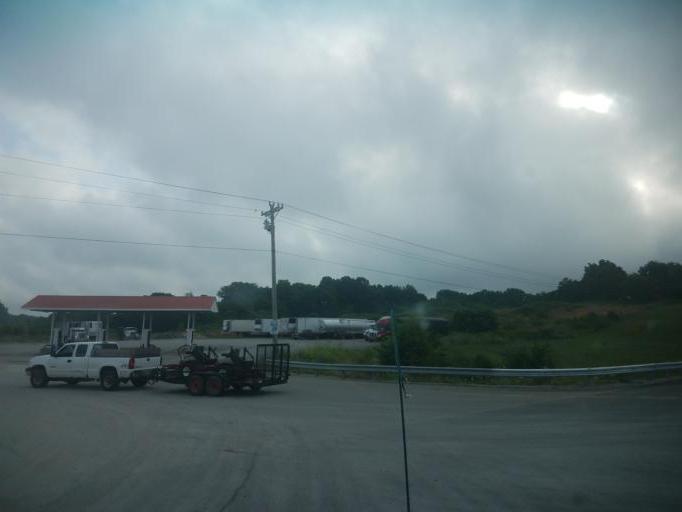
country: US
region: Kentucky
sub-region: Clinton County
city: Albany
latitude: 36.7546
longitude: -85.1360
